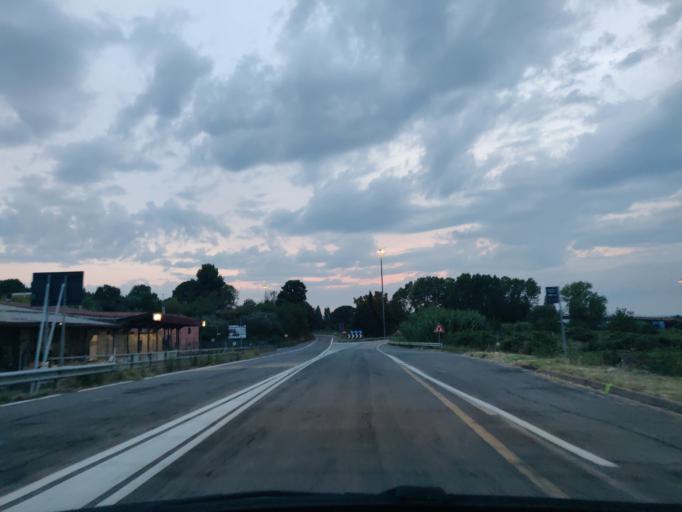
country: IT
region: Latium
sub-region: Provincia di Viterbo
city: Vetralla
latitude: 42.3721
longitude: 12.0610
